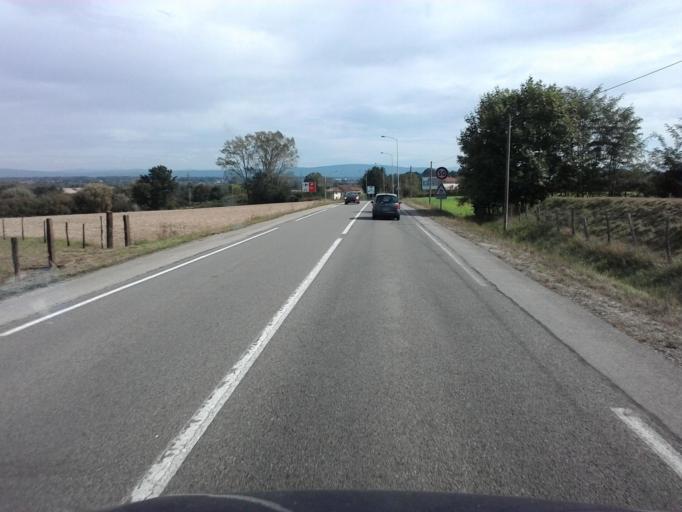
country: FR
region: Rhone-Alpes
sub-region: Departement de l'Ain
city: Viriat
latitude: 46.2335
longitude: 5.1956
